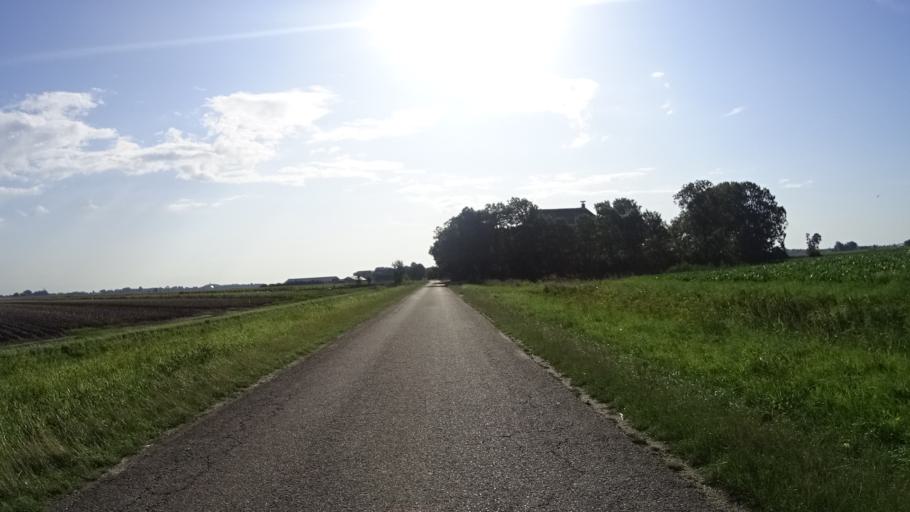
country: NL
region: Friesland
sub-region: Gemeente Harlingen
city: Harlingen
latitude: 53.1231
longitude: 5.4371
